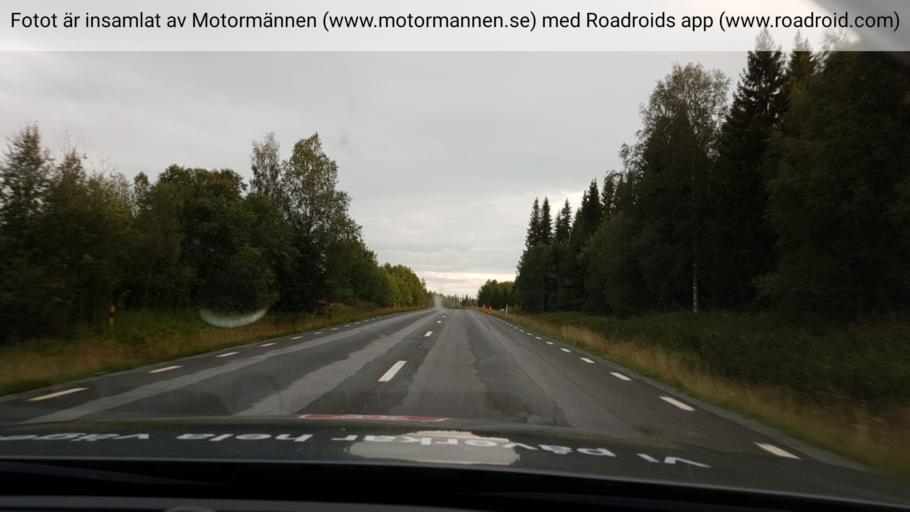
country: SE
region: Jaemtland
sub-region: OEstersunds Kommun
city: Lit
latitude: 63.4661
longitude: 15.1865
